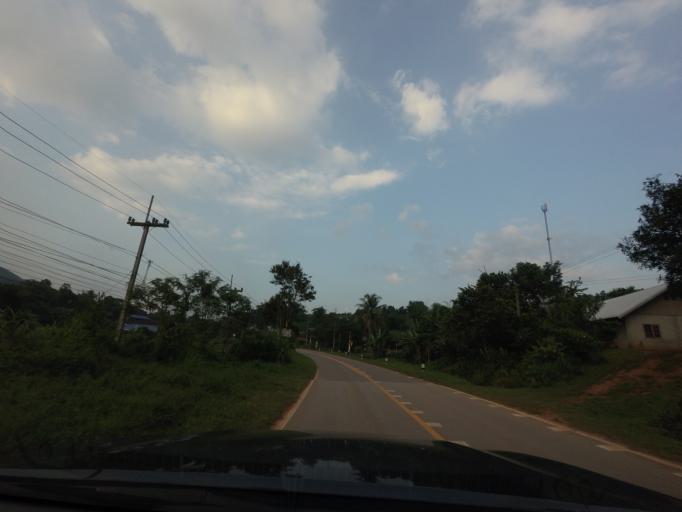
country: TH
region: Loei
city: Na Haeo
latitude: 17.3858
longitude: 101.0453
